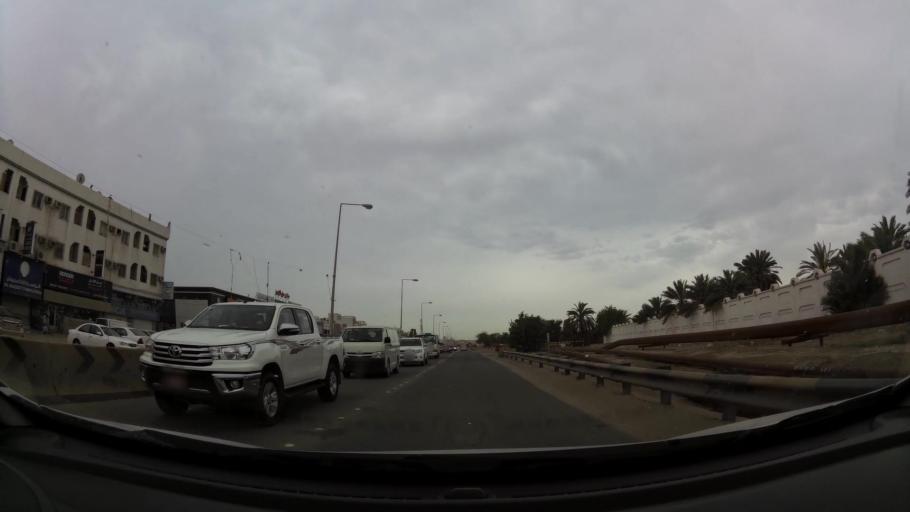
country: BH
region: Central Governorate
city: Madinat Hamad
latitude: 26.1458
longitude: 50.4911
